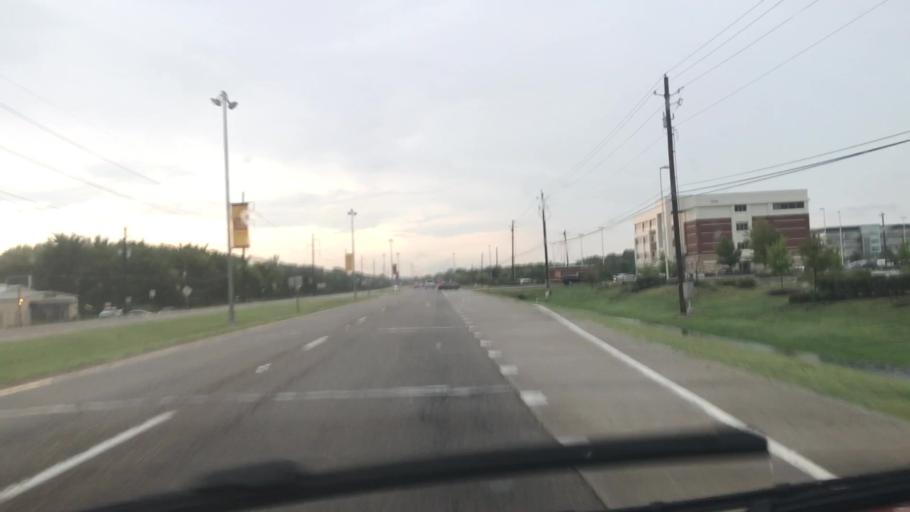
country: US
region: Louisiana
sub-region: Bossier Parish
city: Red Chute
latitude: 32.5414
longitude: -93.6473
